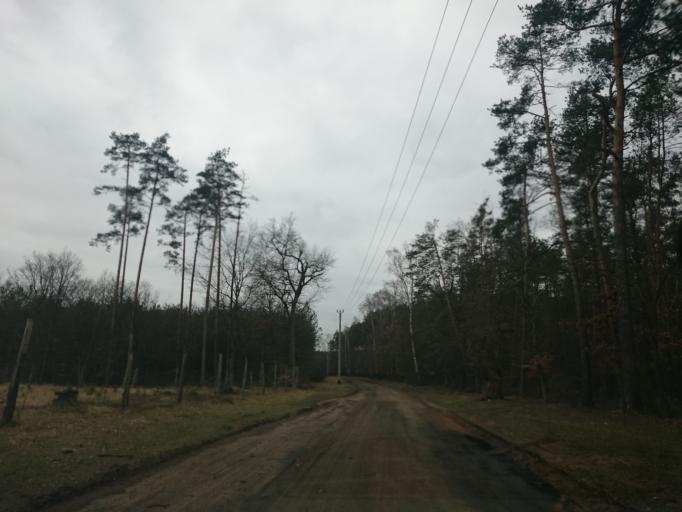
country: PL
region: Kujawsko-Pomorskie
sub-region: Powiat golubsko-dobrzynski
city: Ciechocin
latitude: 53.0751
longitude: 18.9486
